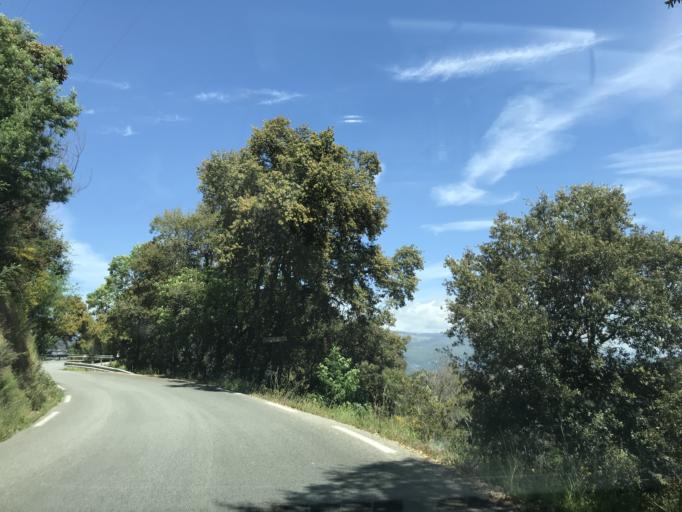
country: FR
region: Provence-Alpes-Cote d'Azur
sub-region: Departement du Var
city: Tanneron
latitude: 43.5853
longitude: 6.8932
